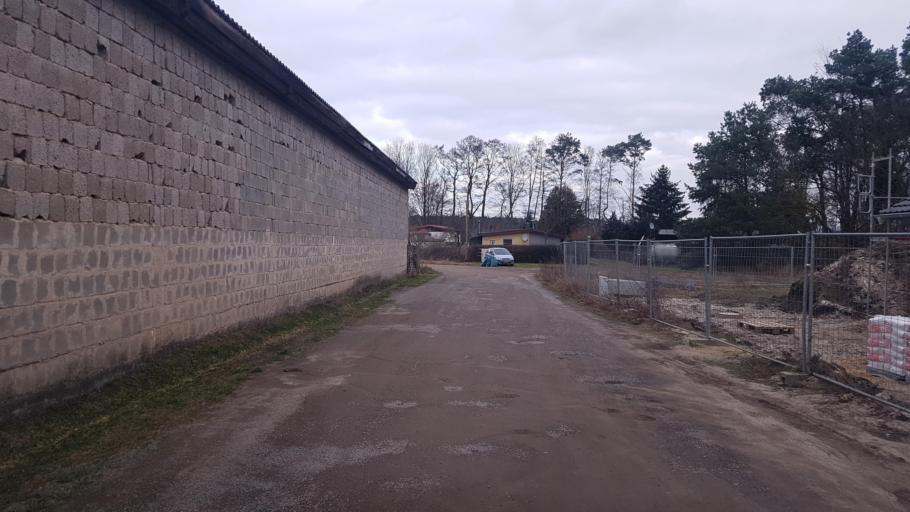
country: DE
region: Brandenburg
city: Halbe
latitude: 52.1111
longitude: 13.6915
